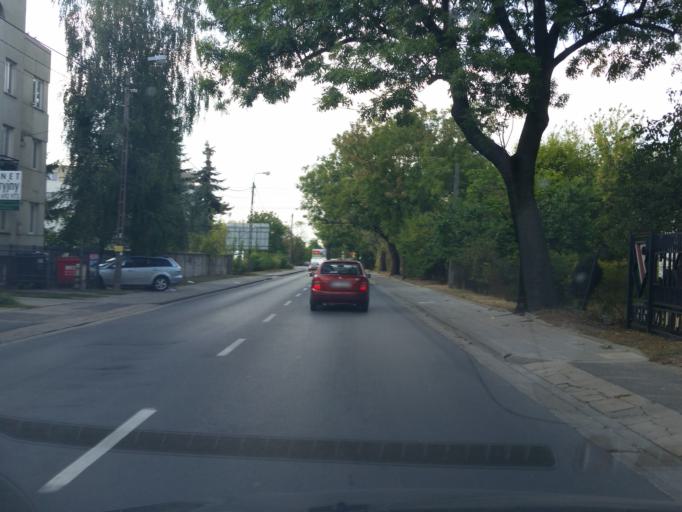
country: PL
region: Masovian Voivodeship
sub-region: Warszawa
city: Ursus
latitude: 52.1983
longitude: 20.8770
